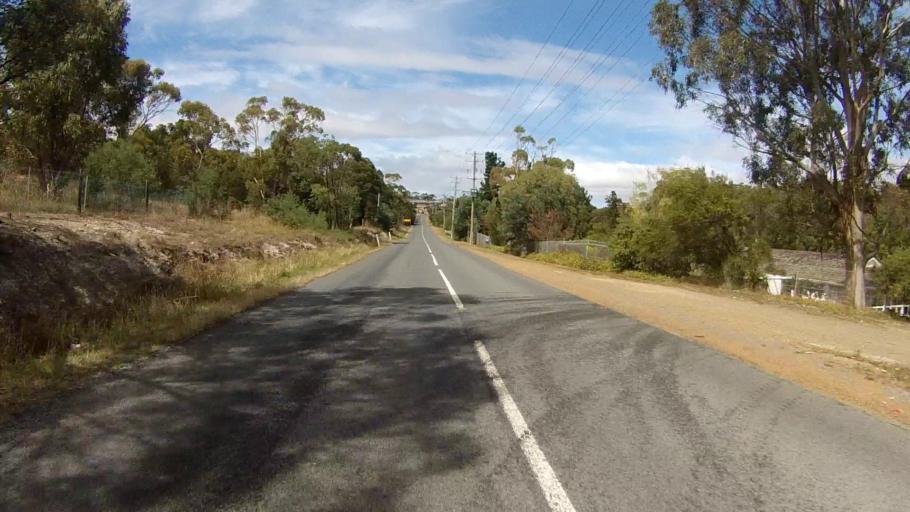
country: AU
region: Tasmania
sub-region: Clarence
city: Lindisfarne
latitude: -42.8167
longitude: 147.3513
